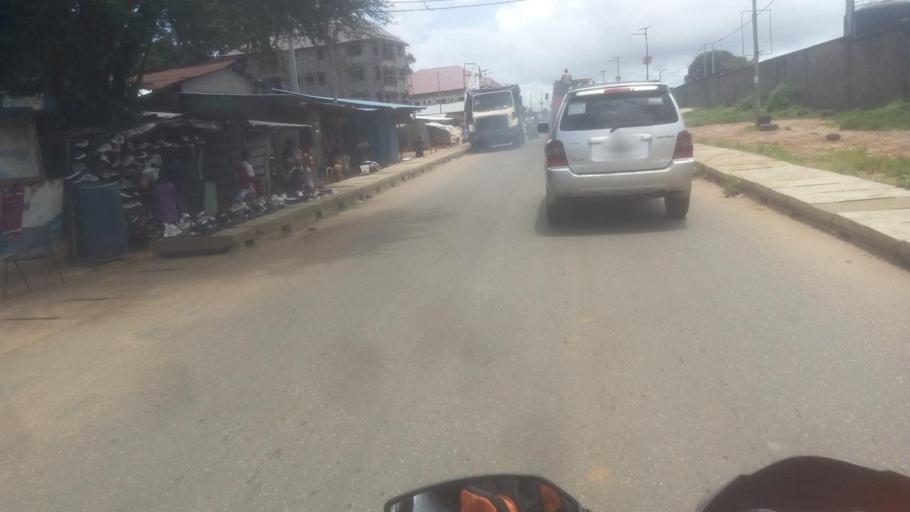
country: SL
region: Northern Province
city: Masoyila
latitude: 8.6137
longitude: -13.2019
